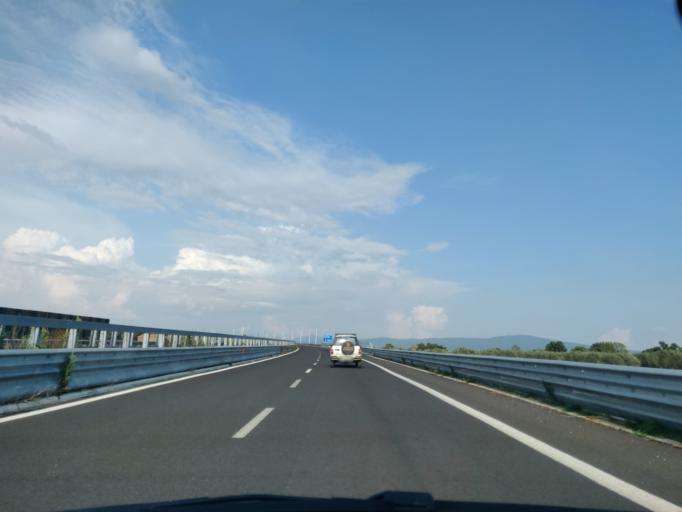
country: IT
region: Latium
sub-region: Provincia di Viterbo
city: Blera
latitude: 42.3036
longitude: 11.9855
